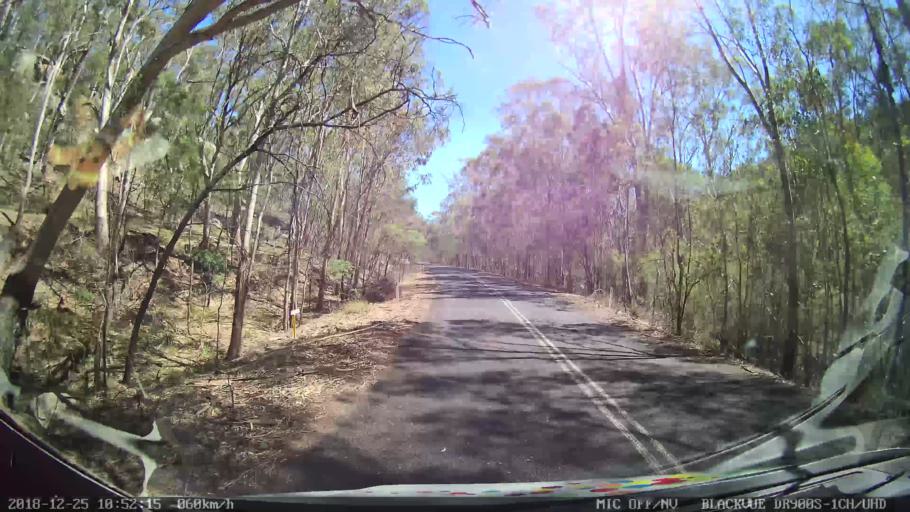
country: AU
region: New South Wales
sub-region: Upper Hunter Shire
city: Merriwa
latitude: -32.4304
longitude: 150.2736
